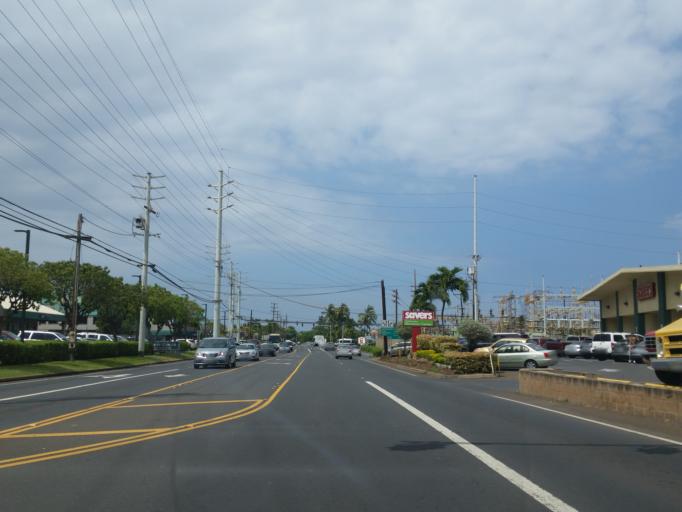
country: US
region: Hawaii
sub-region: Maui County
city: Kahului
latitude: 20.8838
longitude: -156.4537
